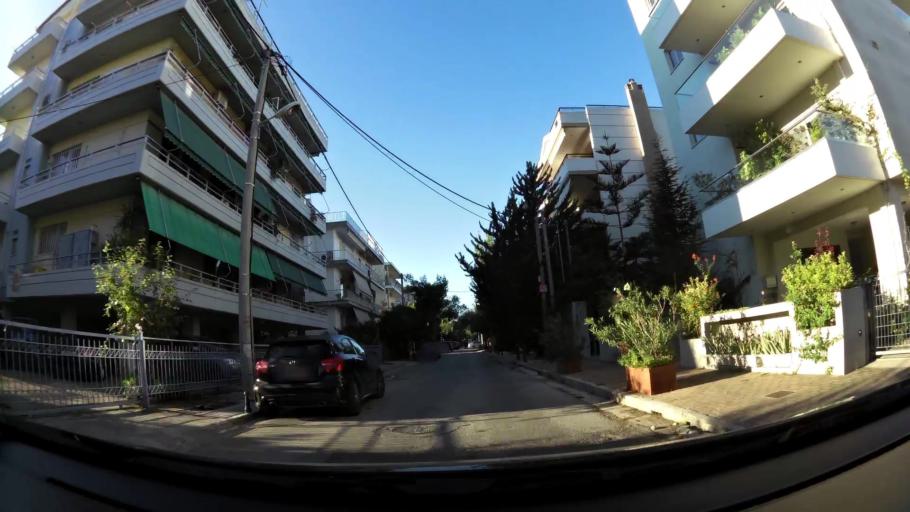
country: GR
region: Attica
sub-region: Nomarchia Athinas
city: Neo Psychiko
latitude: 38.0099
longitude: 23.7903
